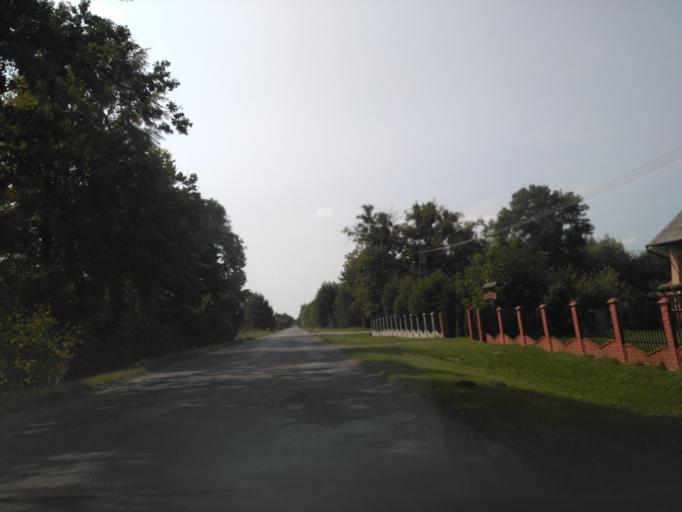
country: PL
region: Lublin Voivodeship
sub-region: Powiat wlodawski
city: Urszulin
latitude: 51.3833
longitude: 23.1835
